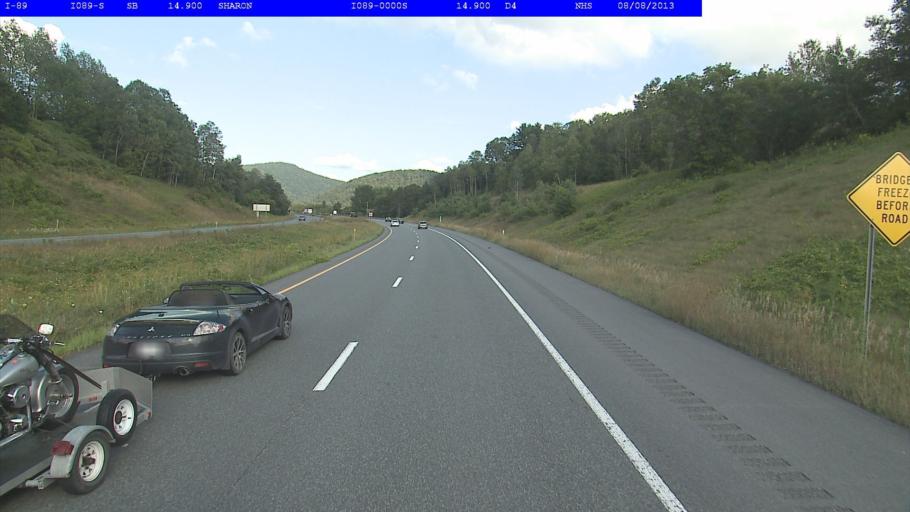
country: US
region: Vermont
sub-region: Windsor County
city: Woodstock
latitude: 43.7821
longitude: -72.4807
